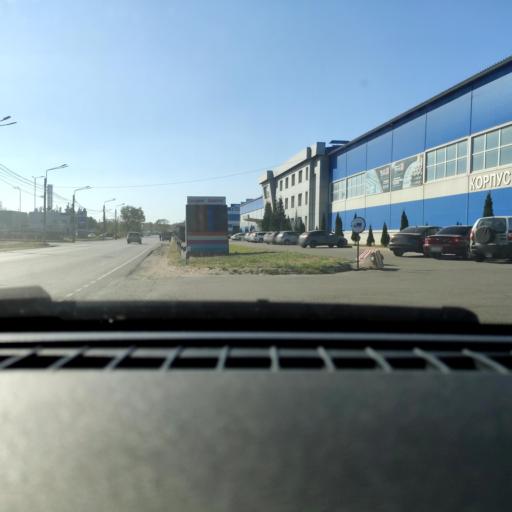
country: RU
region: Voronezj
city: Maslovka
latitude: 51.6380
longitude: 39.2922
